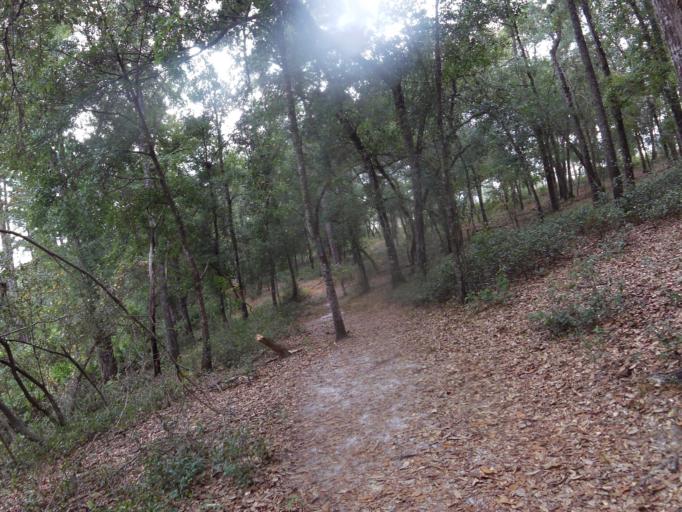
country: US
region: Florida
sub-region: Clay County
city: Keystone Heights
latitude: 29.8312
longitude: -81.9465
